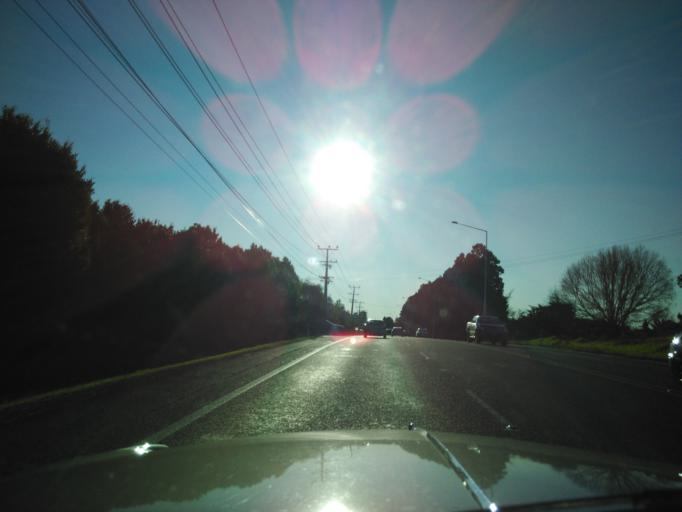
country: NZ
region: Auckland
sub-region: Auckland
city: Rosebank
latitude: -36.7908
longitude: 174.5863
